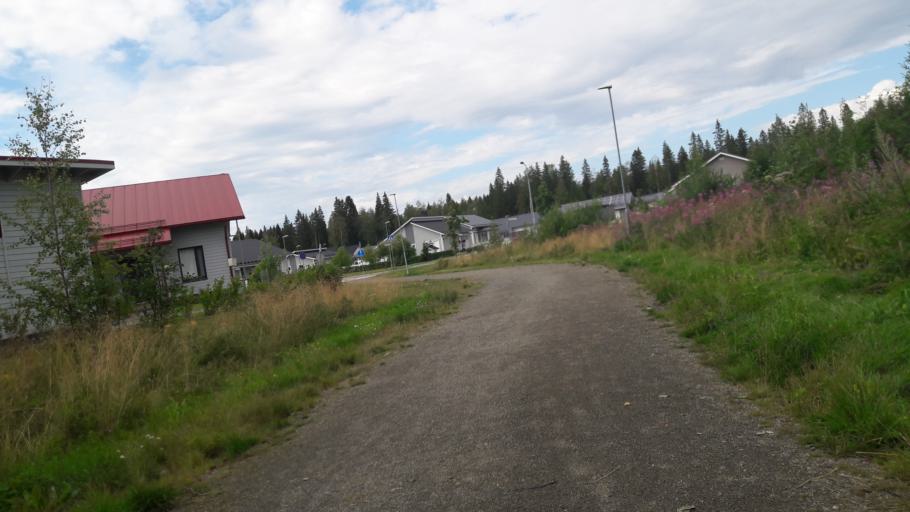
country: FI
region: North Karelia
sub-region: Joensuu
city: Joensuu
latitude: 62.5718
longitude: 29.8258
